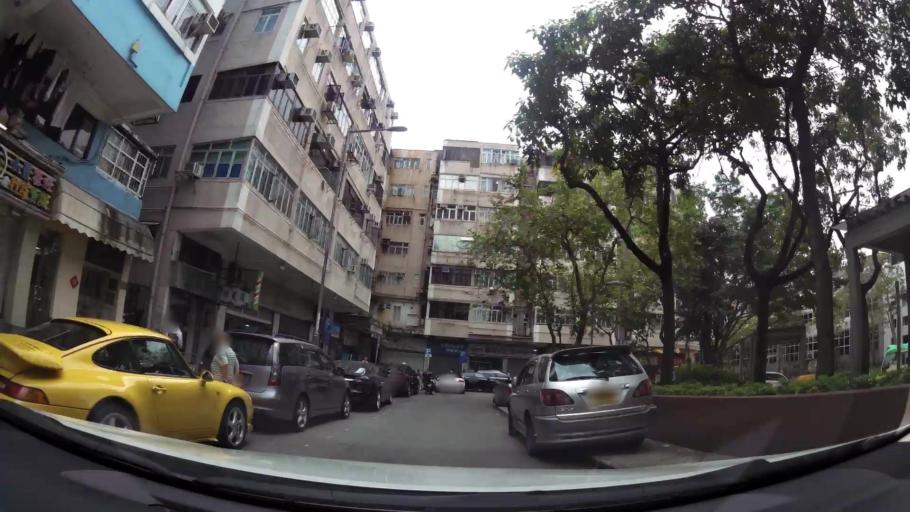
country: HK
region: Wong Tai Sin
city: Wong Tai Sin
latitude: 22.3356
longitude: 114.1879
